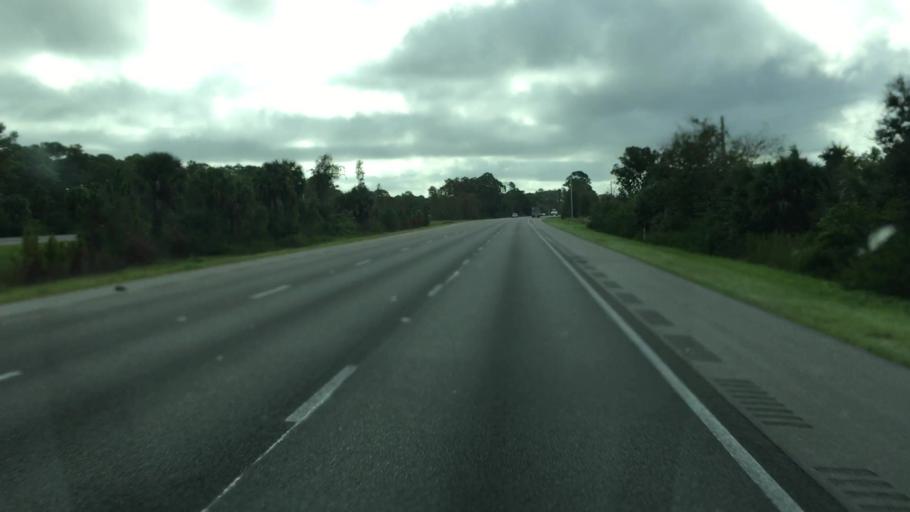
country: US
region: Florida
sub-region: Volusia County
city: Samsula-Spruce Creek
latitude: 29.0712
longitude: -81.0118
